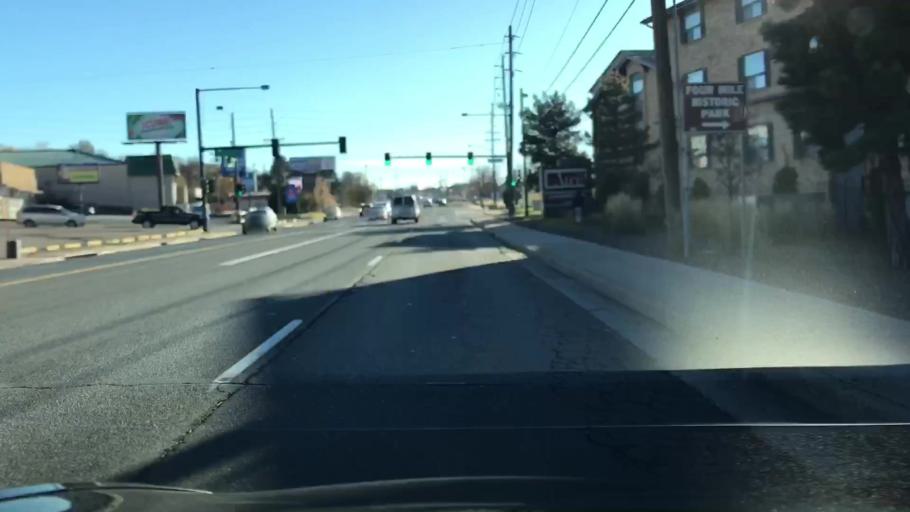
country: US
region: Colorado
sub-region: Arapahoe County
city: Glendale
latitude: 39.7082
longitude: -104.9278
